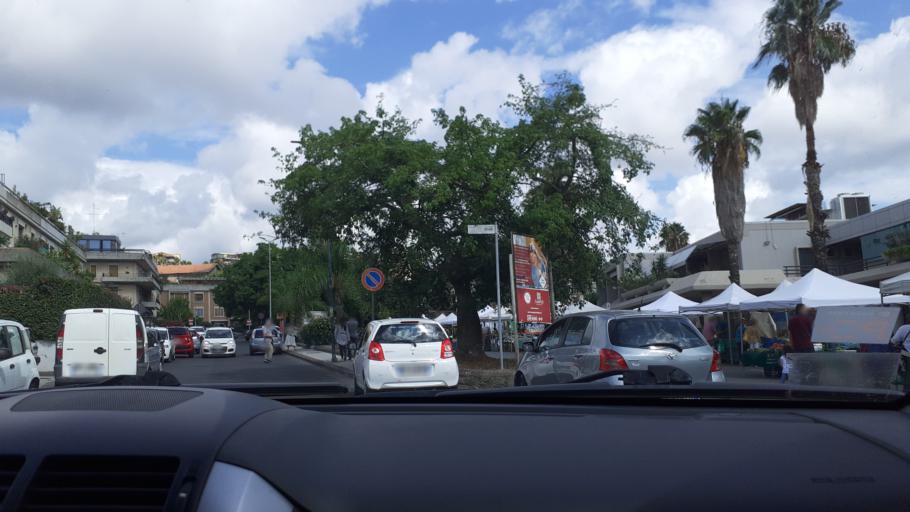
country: IT
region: Sicily
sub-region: Catania
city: Canalicchio
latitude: 37.5400
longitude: 15.0992
